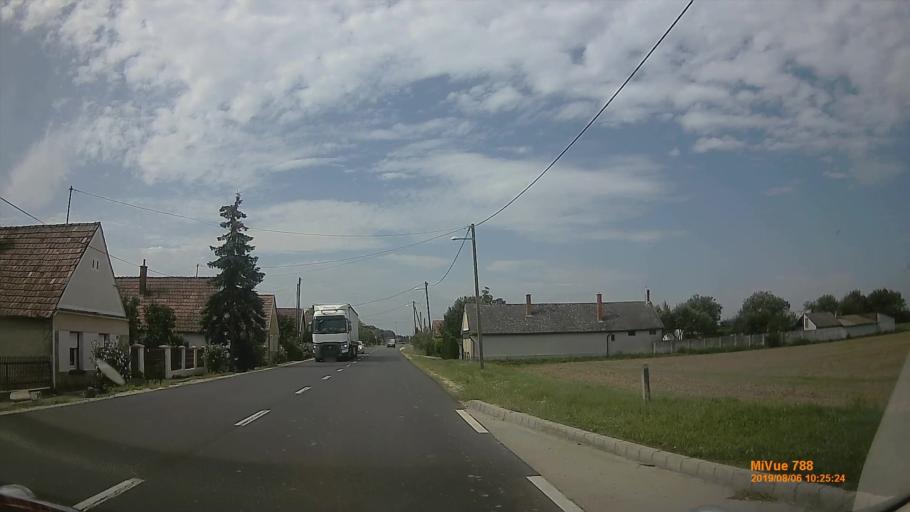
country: HU
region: Vas
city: Kormend
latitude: 47.0526
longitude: 16.6918
